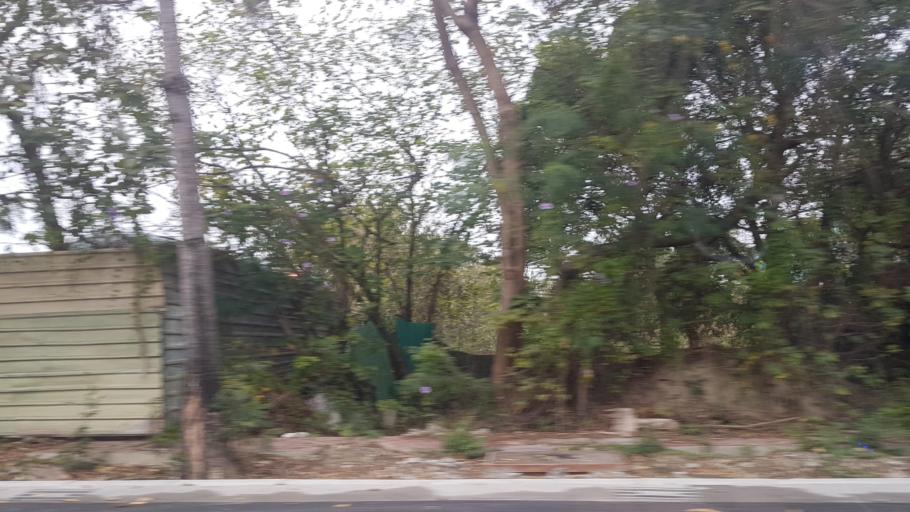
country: TW
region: Taiwan
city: Xinying
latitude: 23.3123
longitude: 120.2985
